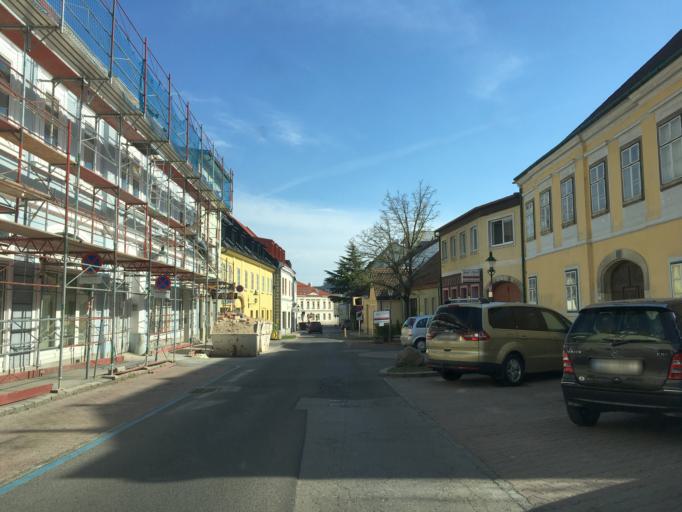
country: AT
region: Lower Austria
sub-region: Politischer Bezirk Modling
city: Brunn am Gebirge
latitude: 48.1066
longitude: 16.2843
